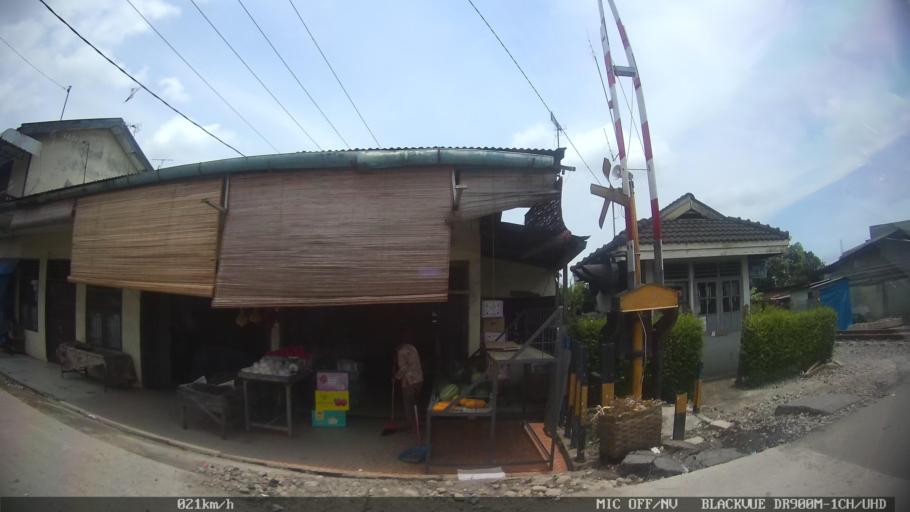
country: ID
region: North Sumatra
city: Labuhan Deli
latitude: 3.6959
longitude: 98.6739
